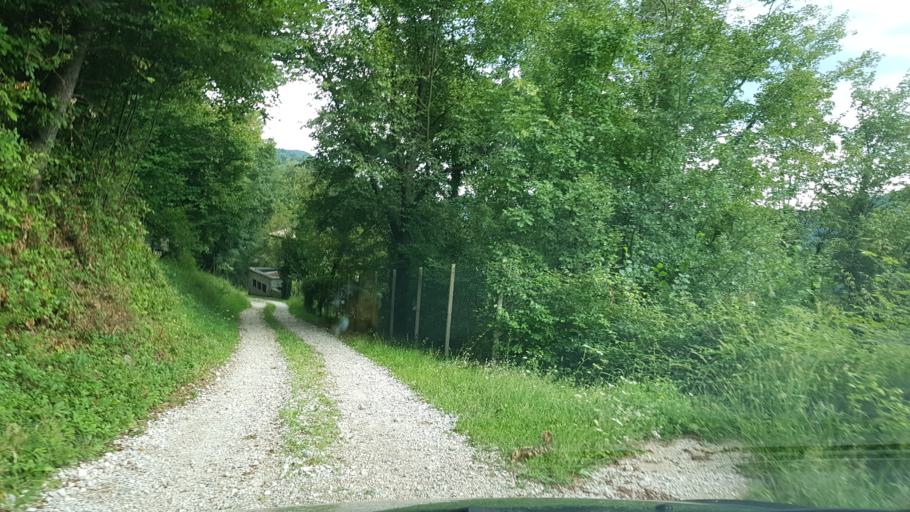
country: SI
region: Kanal
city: Deskle
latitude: 46.0533
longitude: 13.5869
